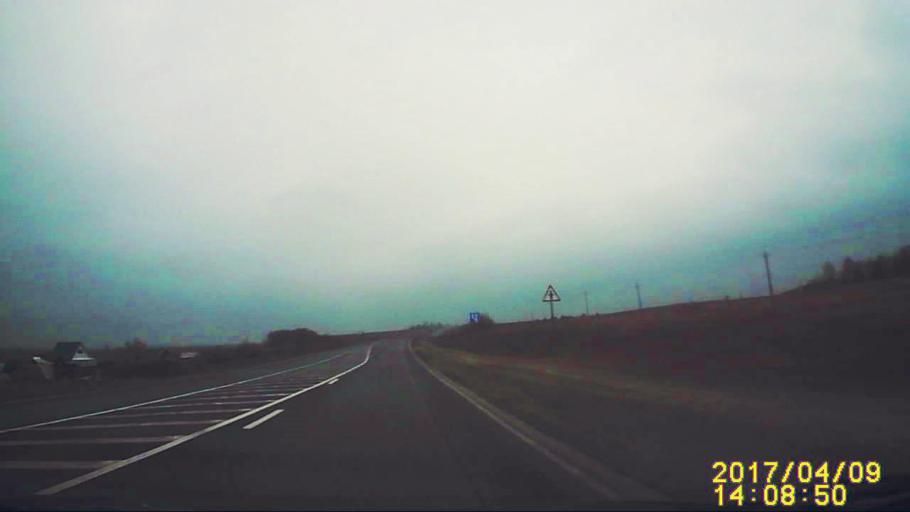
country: RU
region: Ulyanovsk
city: Silikatnyy
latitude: 54.0234
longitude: 48.2145
